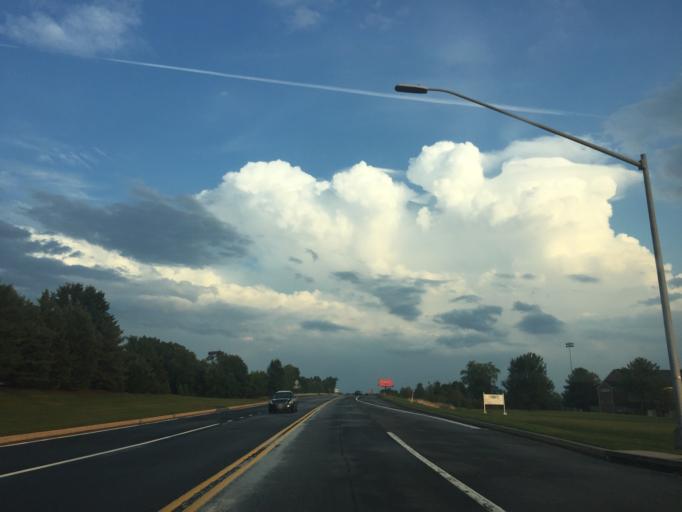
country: US
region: Maryland
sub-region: Harford County
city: Riverside
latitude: 39.4741
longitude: -76.2369
